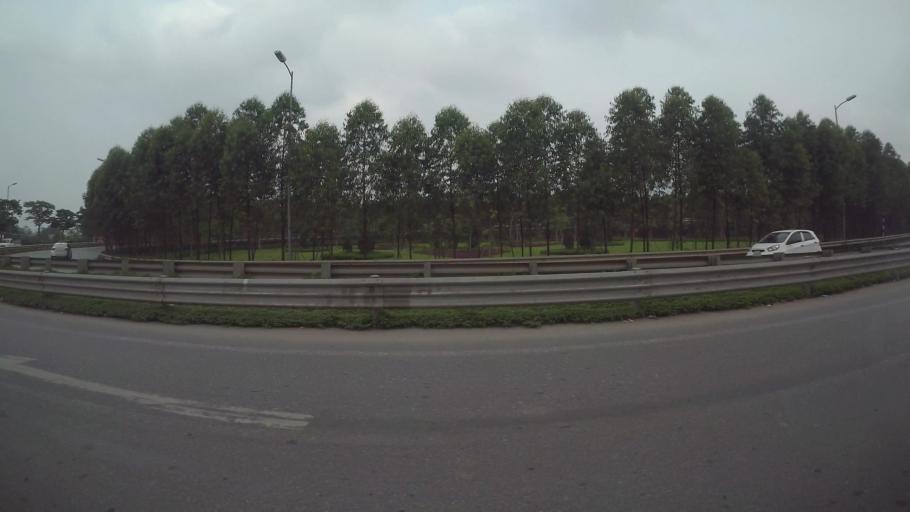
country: VN
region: Ha Noi
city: Trau Quy
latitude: 21.0070
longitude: 105.9121
